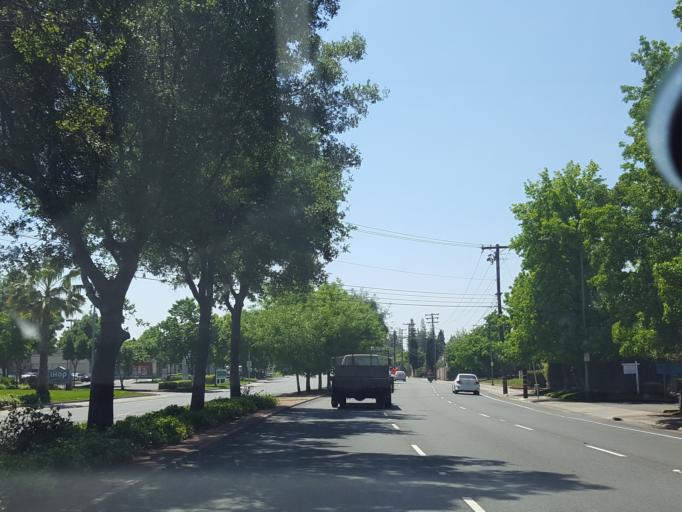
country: US
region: California
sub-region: Sacramento County
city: La Riviera
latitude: 38.5595
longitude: -121.3362
